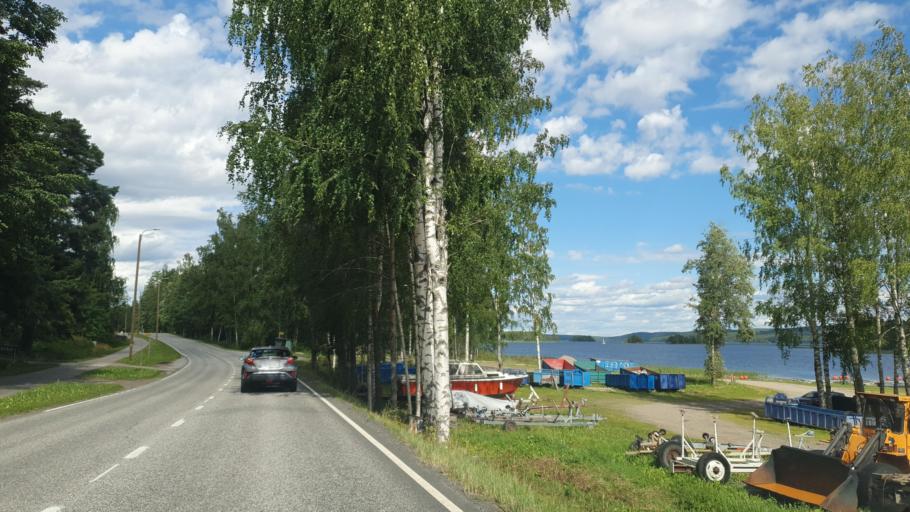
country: FI
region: Central Finland
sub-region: Jyvaeskylae
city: Saeynaetsalo
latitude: 62.1463
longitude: 25.7491
